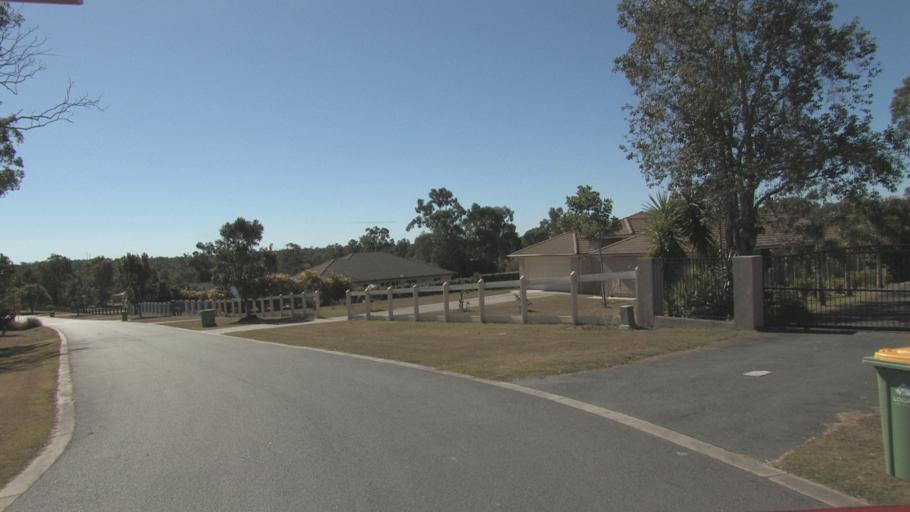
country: AU
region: Queensland
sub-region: Logan
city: North Maclean
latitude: -27.7592
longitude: 152.9642
